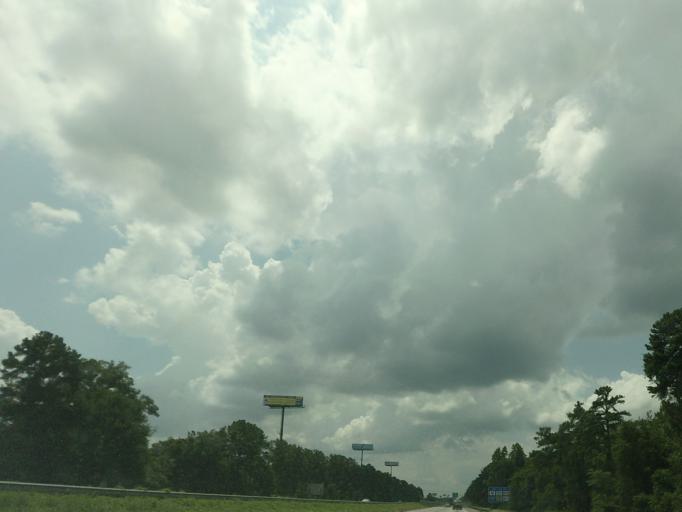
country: US
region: Georgia
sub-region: Peach County
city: Byron
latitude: 32.6340
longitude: -83.7436
